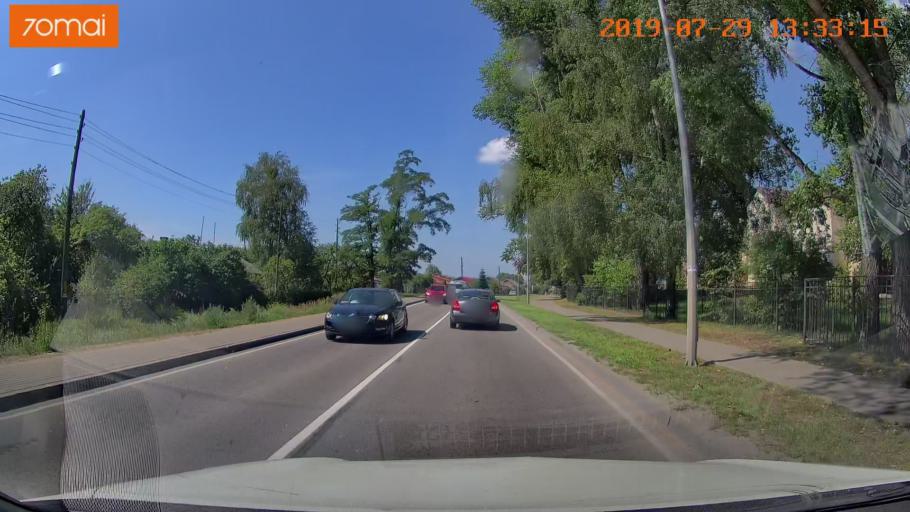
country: RU
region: Kaliningrad
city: Vzmorye
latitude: 54.6984
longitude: 20.2285
